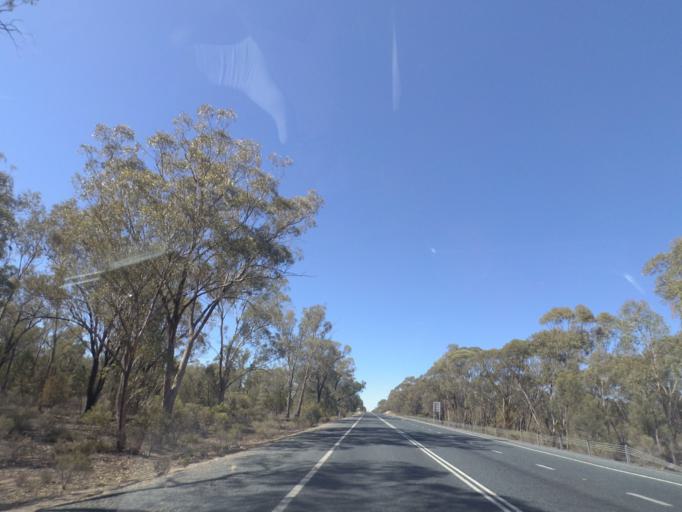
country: AU
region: New South Wales
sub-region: Bland
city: West Wyalong
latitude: -34.1256
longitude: 147.1256
